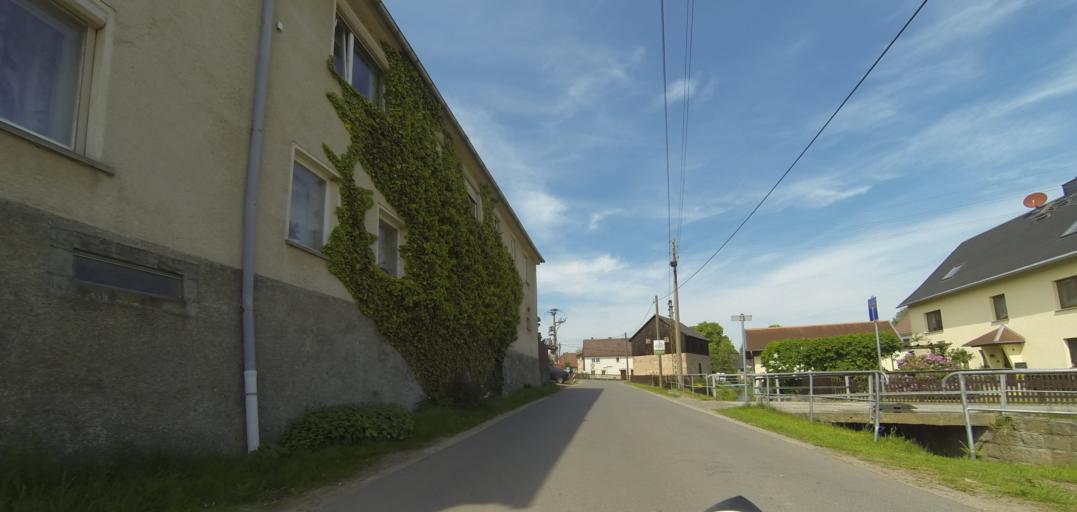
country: DE
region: Saxony
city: Grossrohrsdorf
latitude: 51.1009
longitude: 14.0351
